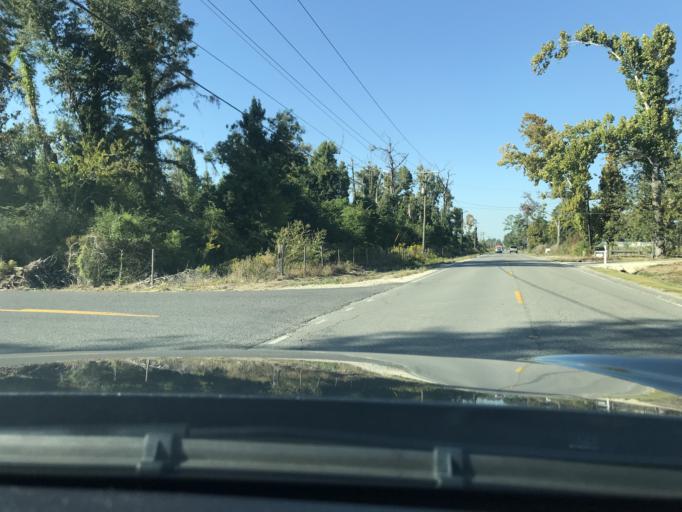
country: US
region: Louisiana
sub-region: Calcasieu Parish
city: Moss Bluff
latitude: 30.3152
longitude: -93.2583
